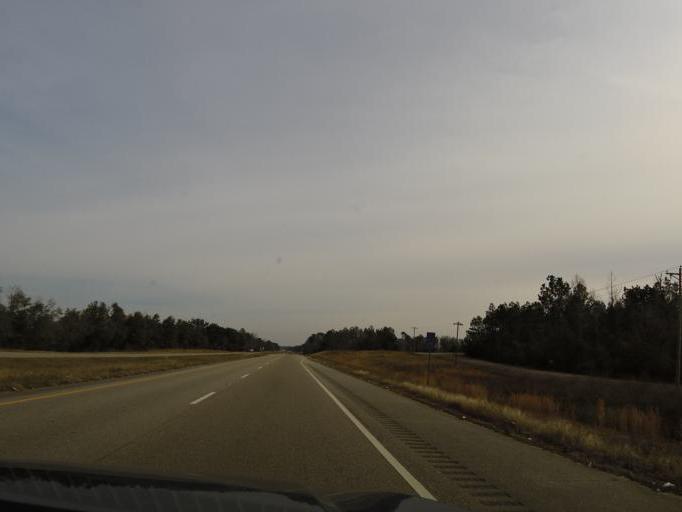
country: US
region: Alabama
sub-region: Houston County
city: Ashford
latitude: 31.1311
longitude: -85.0845
